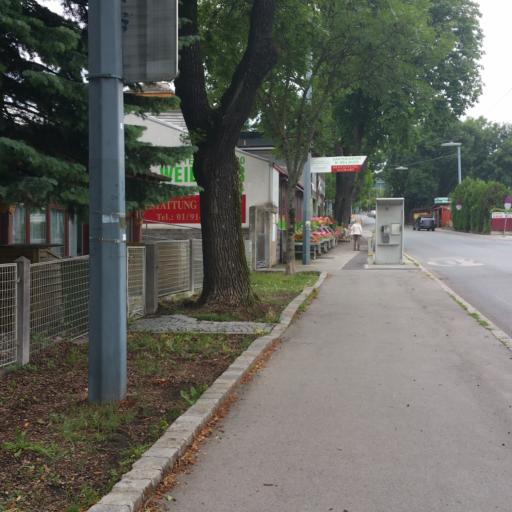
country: AT
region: Vienna
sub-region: Wien Stadt
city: Vienna
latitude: 48.2141
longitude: 16.3012
